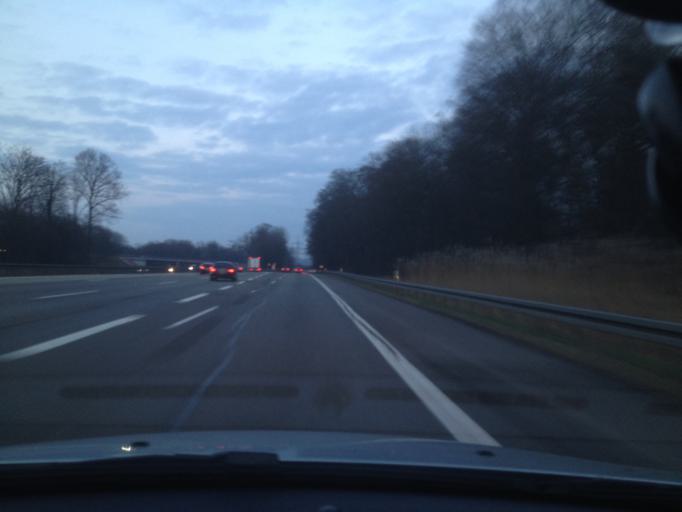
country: DE
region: Baden-Wuerttemberg
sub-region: Karlsruhe Region
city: Ettlingen
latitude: 48.9694
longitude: 8.4313
